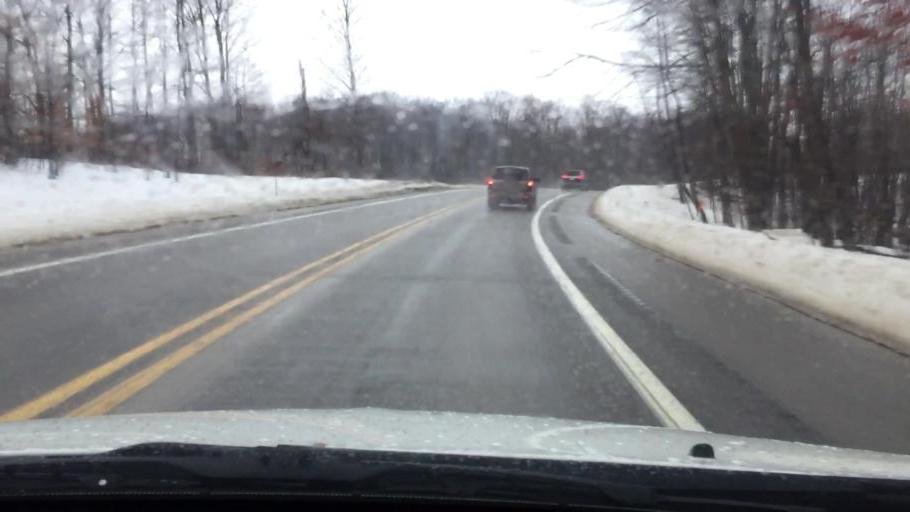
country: US
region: Michigan
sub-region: Charlevoix County
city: East Jordan
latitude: 45.2085
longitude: -85.1668
